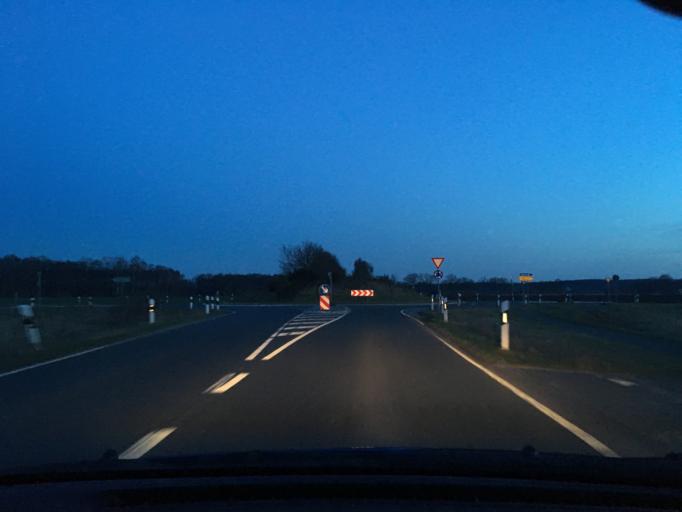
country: DE
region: Lower Saxony
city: Oldendorf
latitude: 53.1781
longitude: 10.2104
